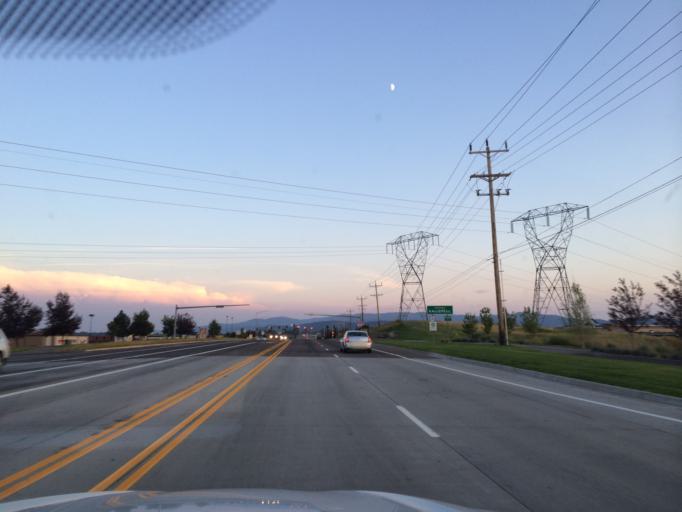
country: US
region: Montana
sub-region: Flathead County
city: Kalispell
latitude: 48.2400
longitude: -114.3306
